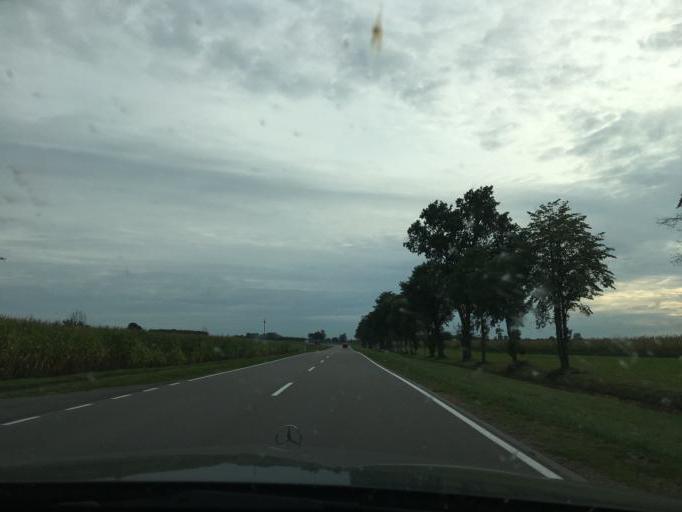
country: PL
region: Masovian Voivodeship
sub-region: Powiat ostrowski
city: Ostrow Mazowiecka
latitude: 52.8887
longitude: 21.8661
